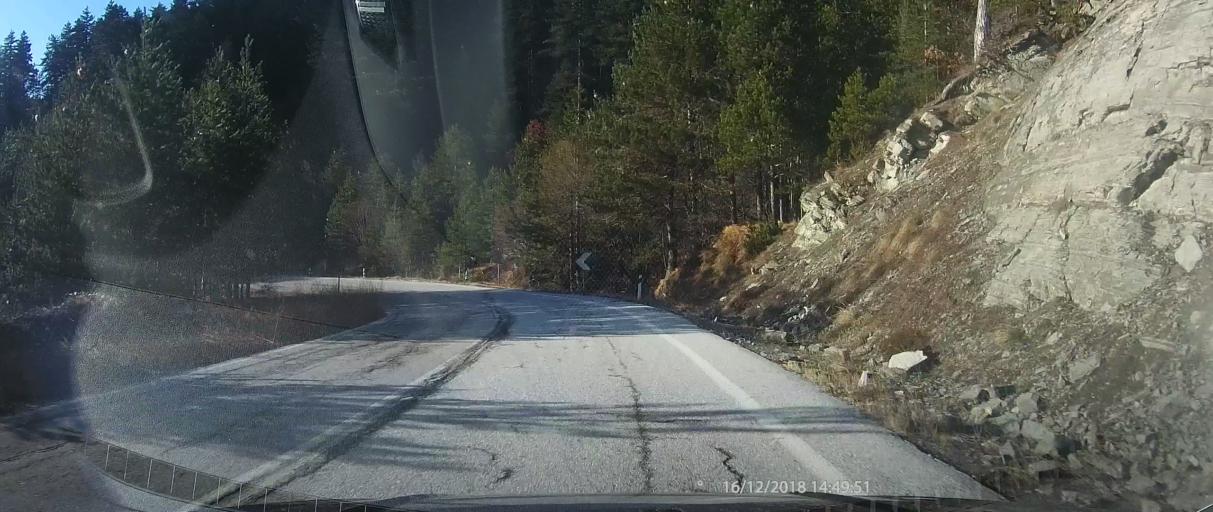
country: GR
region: West Macedonia
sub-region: Nomos Kastorias
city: Nestorio
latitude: 40.2098
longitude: 21.0840
